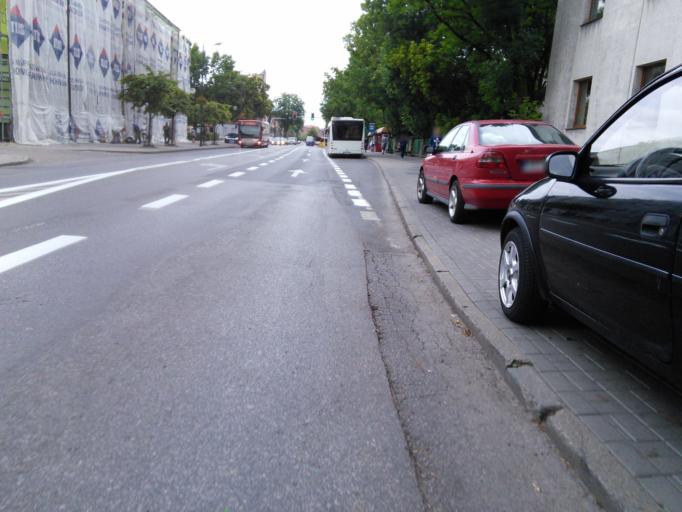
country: PL
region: Silesian Voivodeship
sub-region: Piekary Slaskie
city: Piekary Slaskie
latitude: 50.3768
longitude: 18.9438
